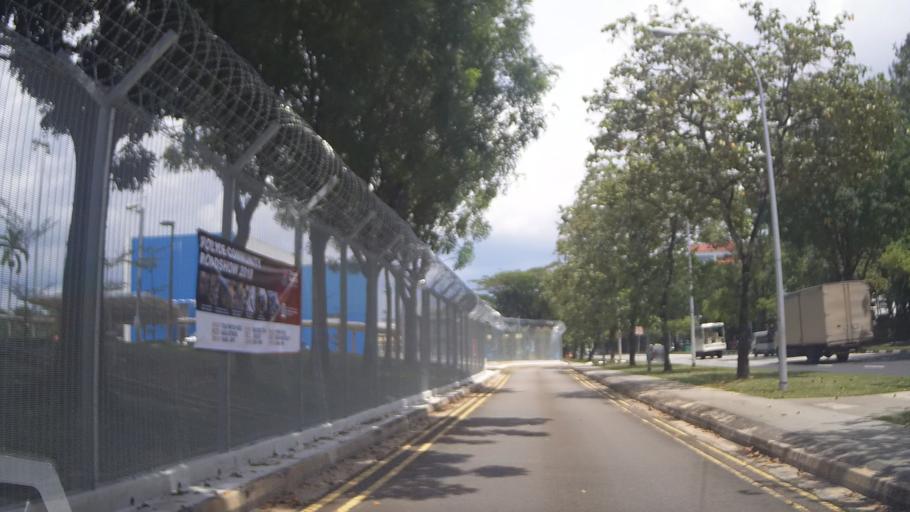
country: MY
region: Johor
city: Johor Bahru
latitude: 1.3967
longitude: 103.7426
